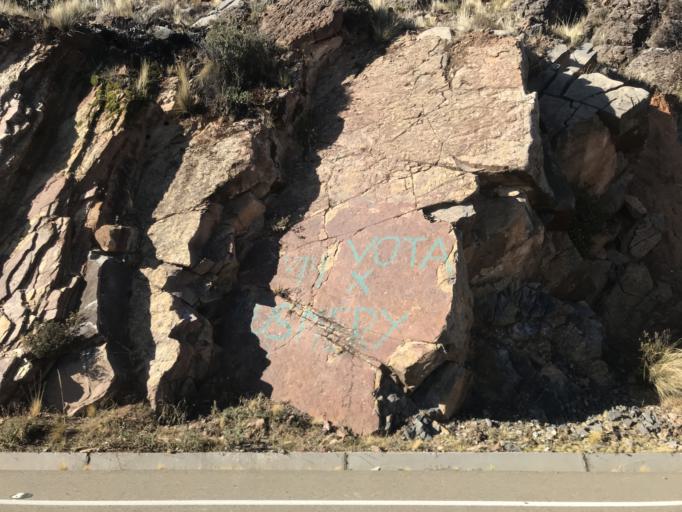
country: BO
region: La Paz
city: San Pedro
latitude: -16.1917
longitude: -68.9165
